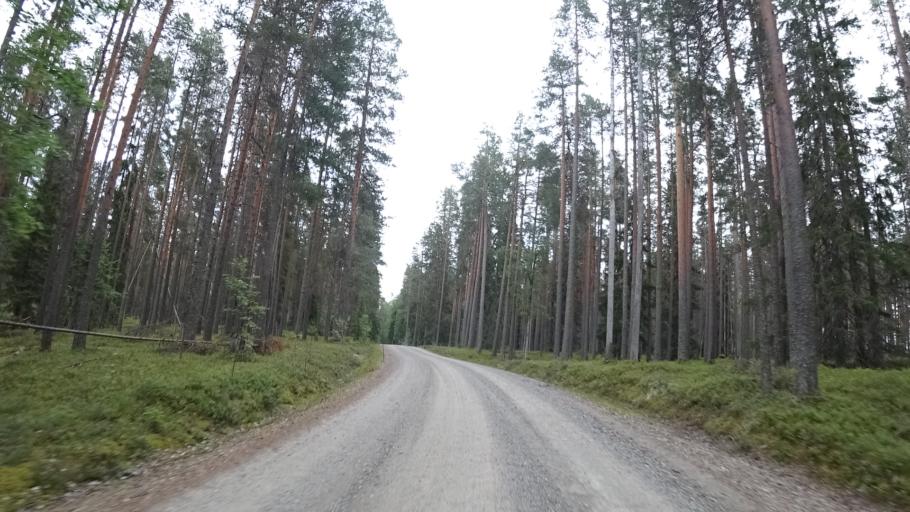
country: FI
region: North Karelia
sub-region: Joensuu
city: Ilomantsi
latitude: 62.5836
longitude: 31.1696
